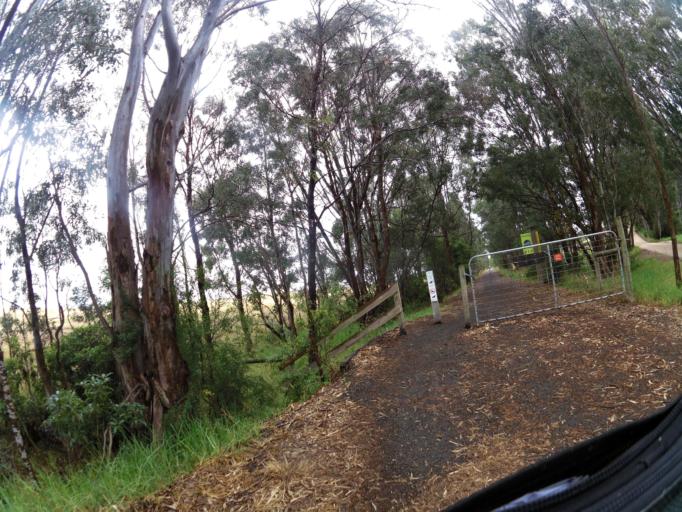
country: AU
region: Victoria
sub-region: East Gippsland
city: Bairnsdale
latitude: -37.8184
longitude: 147.7263
